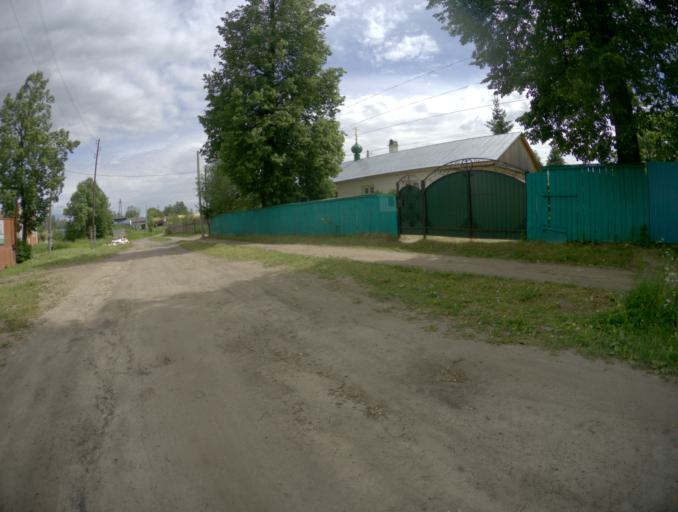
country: RU
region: Ivanovo
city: Savino
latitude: 56.5894
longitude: 41.2095
